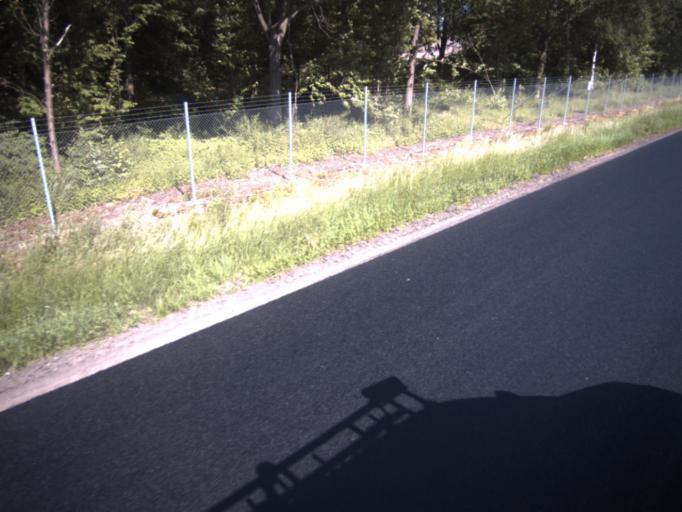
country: SE
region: Skane
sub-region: Helsingborg
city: Odakra
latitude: 56.0674
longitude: 12.7589
